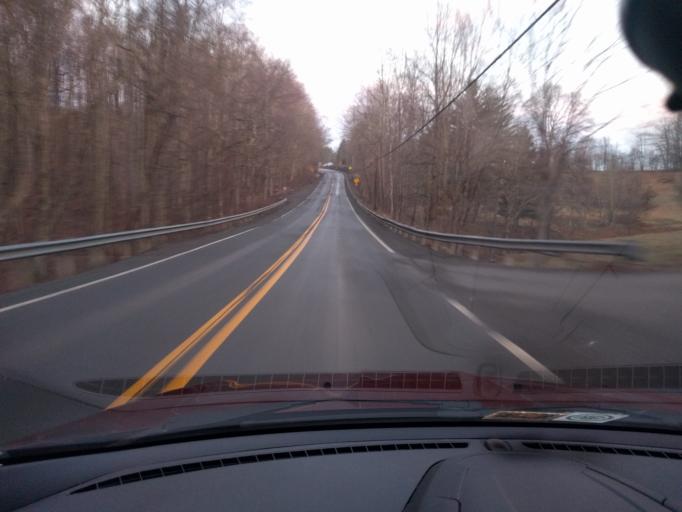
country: US
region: West Virginia
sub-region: Greenbrier County
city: Rainelle
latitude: 38.0096
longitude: -80.8806
